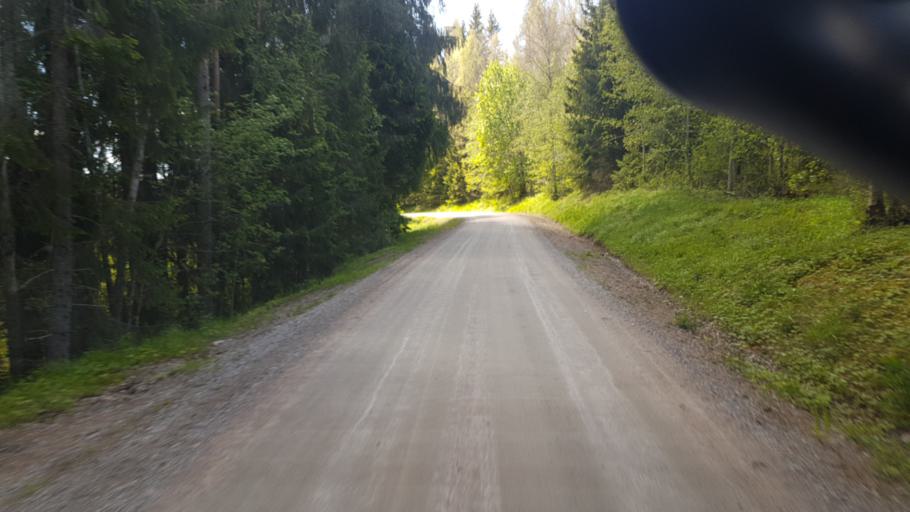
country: SE
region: Vaermland
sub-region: Arvika Kommun
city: Arvika
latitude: 59.6828
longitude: 12.7716
